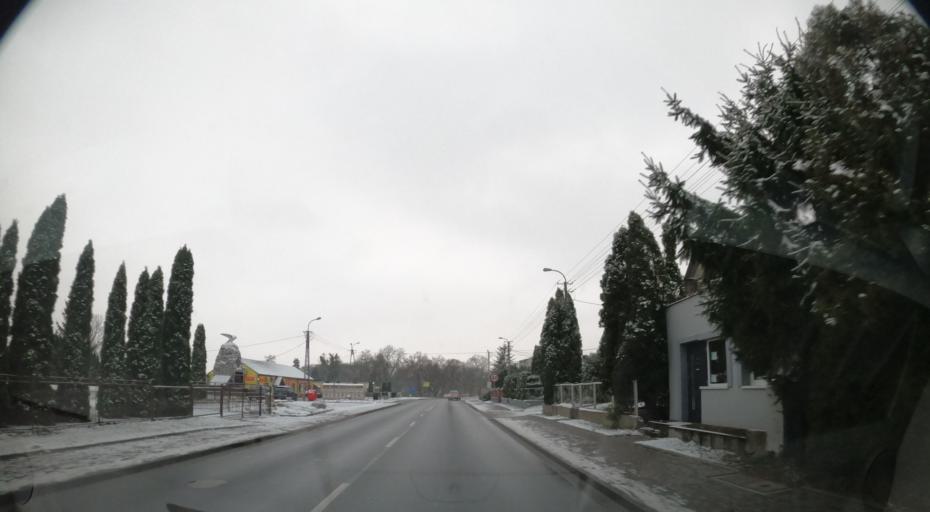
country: PL
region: Kujawsko-Pomorskie
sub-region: Powiat lipnowski
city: Wielgie
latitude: 52.7409
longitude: 19.2627
